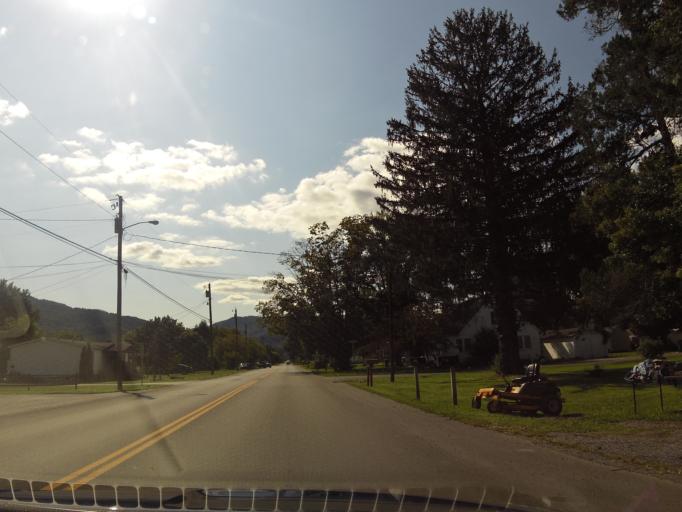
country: US
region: Kentucky
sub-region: Bell County
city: Middlesboro
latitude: 36.6038
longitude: -83.7276
